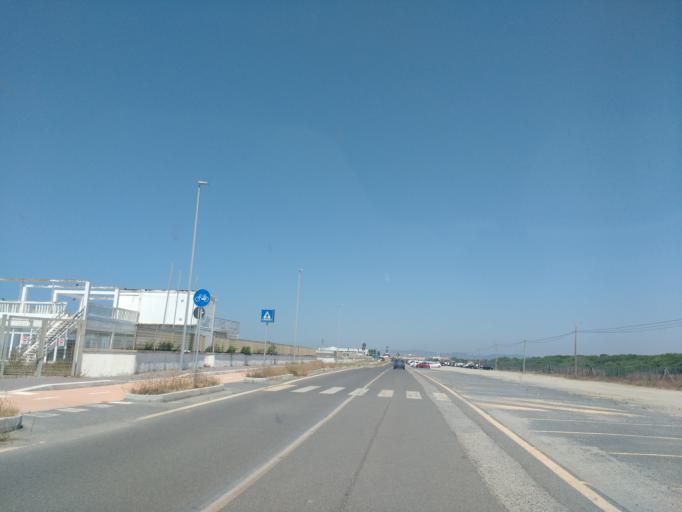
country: IT
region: Latium
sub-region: Citta metropolitana di Roma Capitale
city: Passo Oscuro
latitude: 41.8835
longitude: 12.1722
